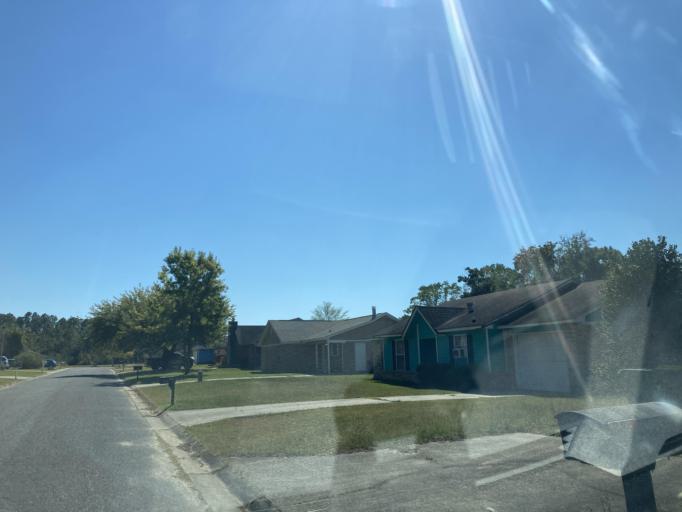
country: US
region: Mississippi
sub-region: Jackson County
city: Saint Martin
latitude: 30.4572
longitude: -88.8630
